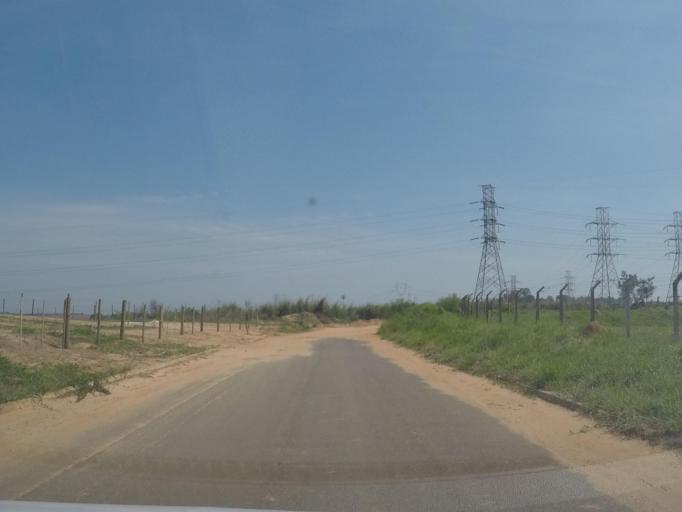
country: BR
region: Sao Paulo
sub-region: Sumare
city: Sumare
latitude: -22.8678
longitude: -47.2846
